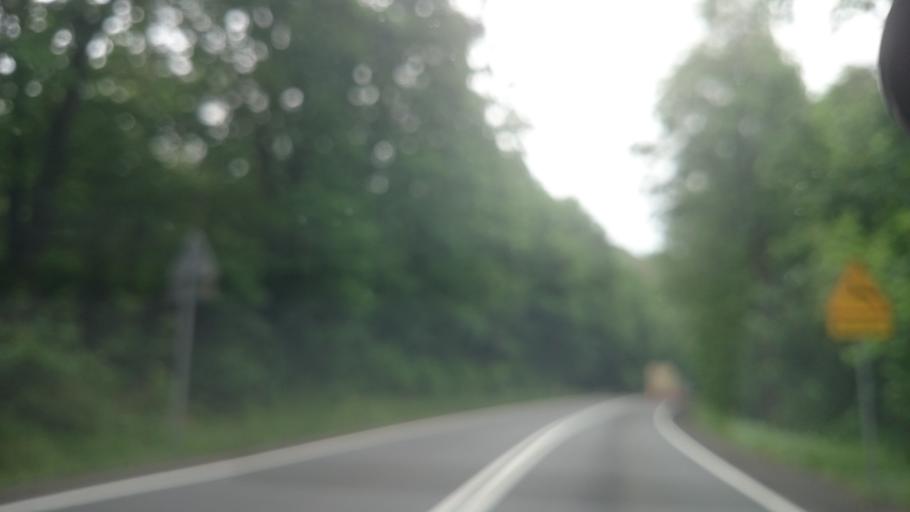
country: PL
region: Lower Silesian Voivodeship
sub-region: Powiat zabkowicki
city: Zloty Stok
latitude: 50.4387
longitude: 16.8230
